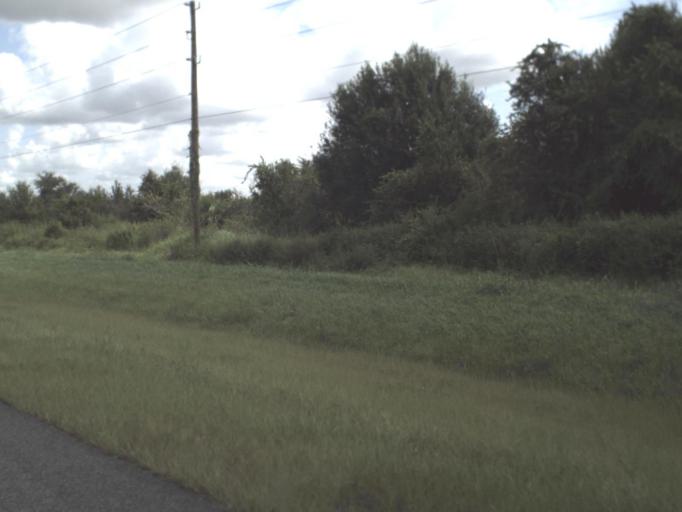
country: US
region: Florida
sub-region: Charlotte County
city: Harbour Heights
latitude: 27.0728
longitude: -81.9581
